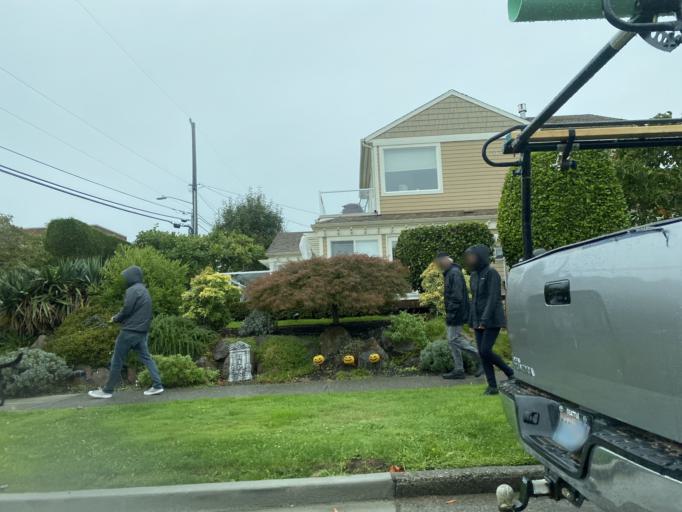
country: US
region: Washington
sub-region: King County
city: Seattle
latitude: 47.6413
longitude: -122.3917
